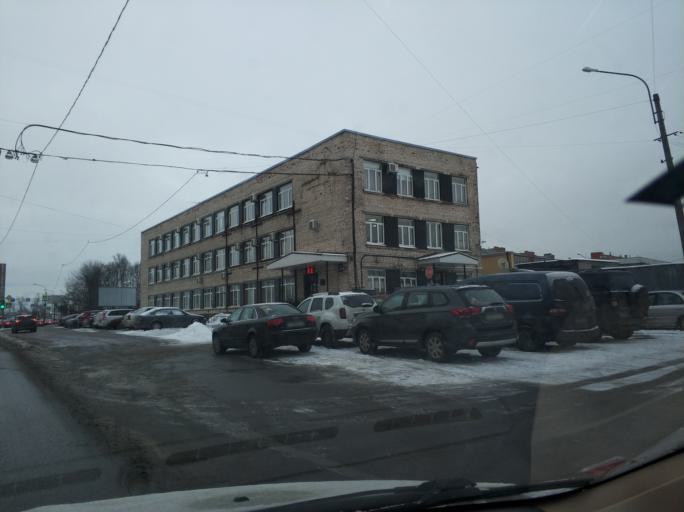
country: RU
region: St.-Petersburg
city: Centralniy
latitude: 59.9177
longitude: 30.3743
